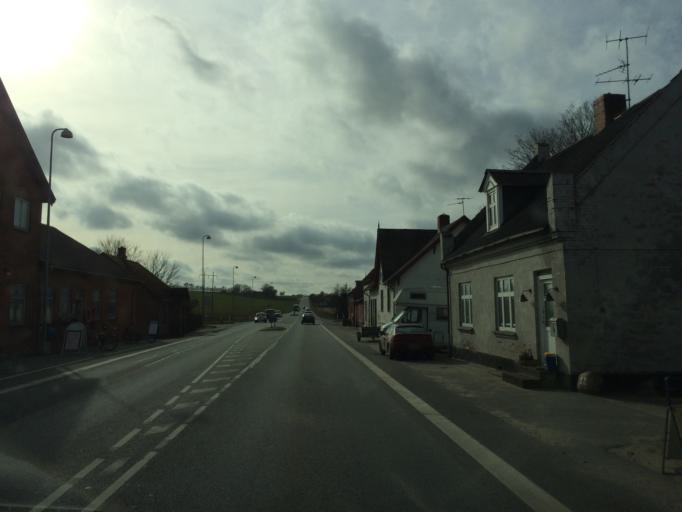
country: DK
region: Central Jutland
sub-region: Norddjurs Kommune
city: Allingabro
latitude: 56.4466
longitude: 10.2811
